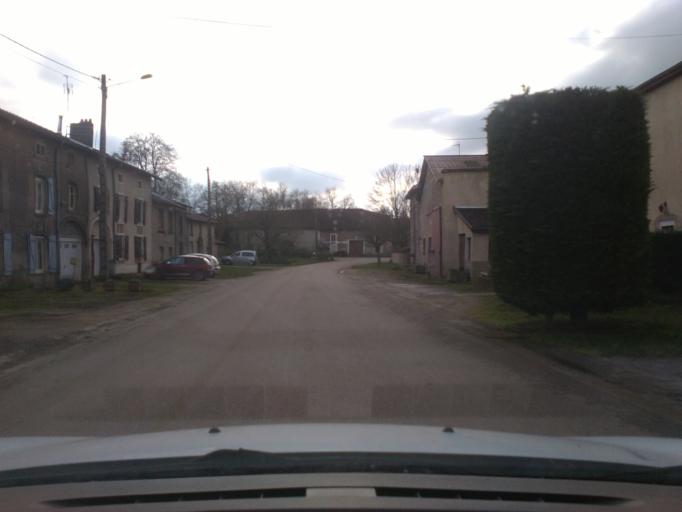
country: FR
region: Lorraine
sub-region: Departement des Vosges
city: Vittel
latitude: 48.3249
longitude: 5.9847
